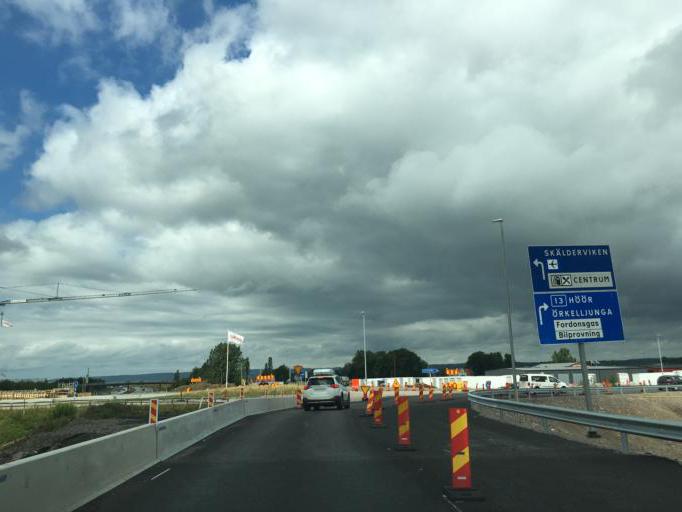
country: SE
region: Skane
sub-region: Angelholms Kommun
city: AEngelholm
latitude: 56.2511
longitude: 12.8992
